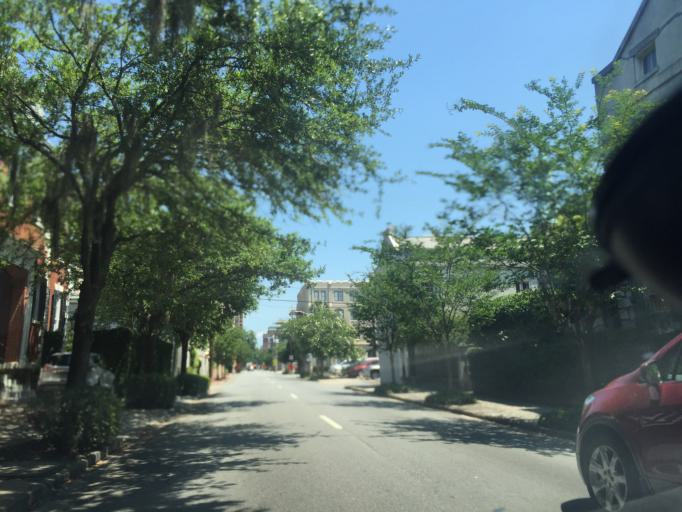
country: US
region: Georgia
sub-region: Chatham County
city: Savannah
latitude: 32.0700
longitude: -81.0941
